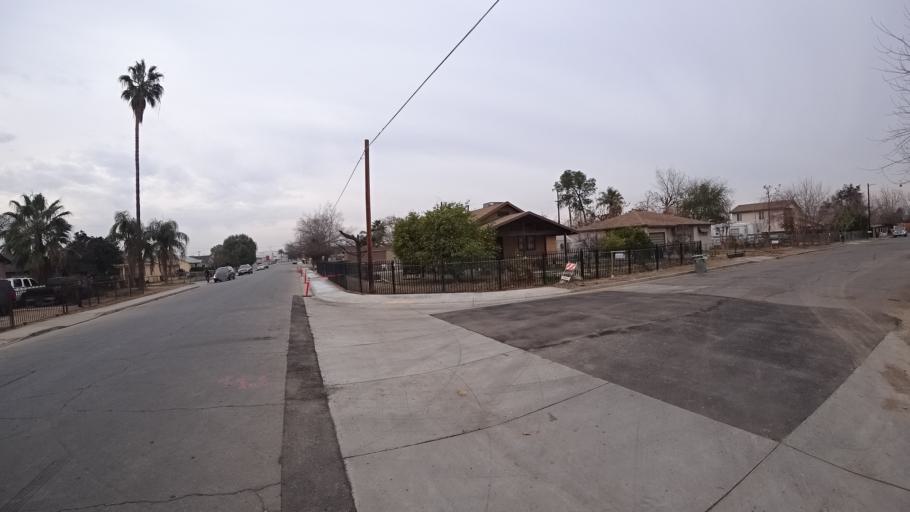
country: US
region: California
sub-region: Kern County
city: Bakersfield
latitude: 35.3576
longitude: -118.9999
